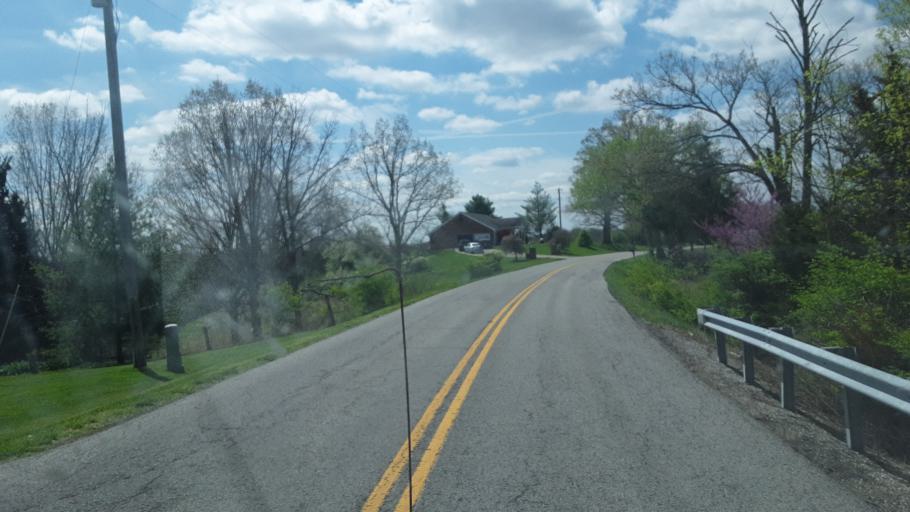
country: US
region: Kentucky
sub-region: Grant County
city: Dry Ridge
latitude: 38.6531
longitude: -84.7027
